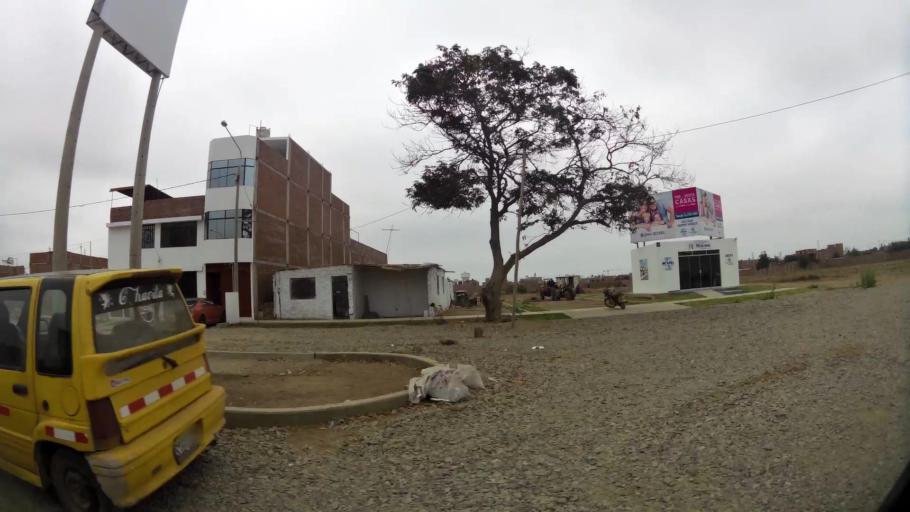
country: PE
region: La Libertad
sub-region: Provincia de Trujillo
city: La Esperanza
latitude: -8.0849
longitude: -79.0495
